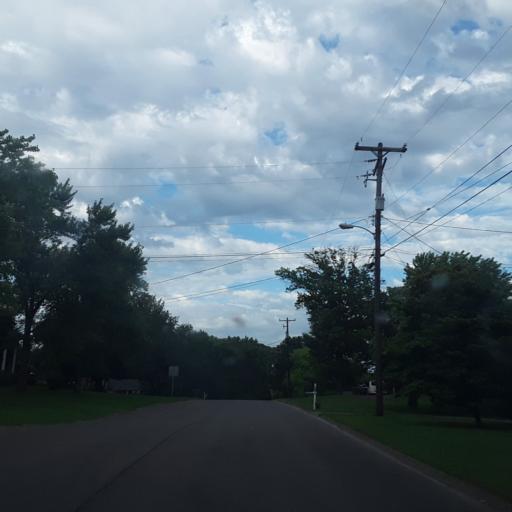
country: US
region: Tennessee
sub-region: Wilson County
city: Green Hill
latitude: 36.1673
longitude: -86.5887
